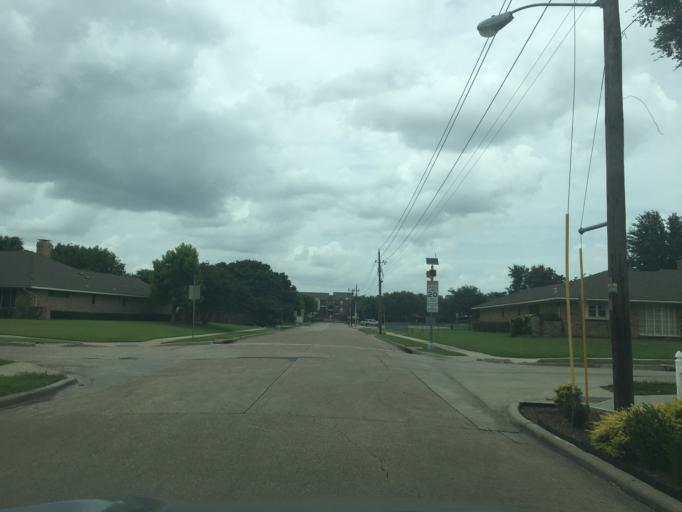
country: US
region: Texas
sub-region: Dallas County
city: Richardson
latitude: 32.9310
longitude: -96.7279
